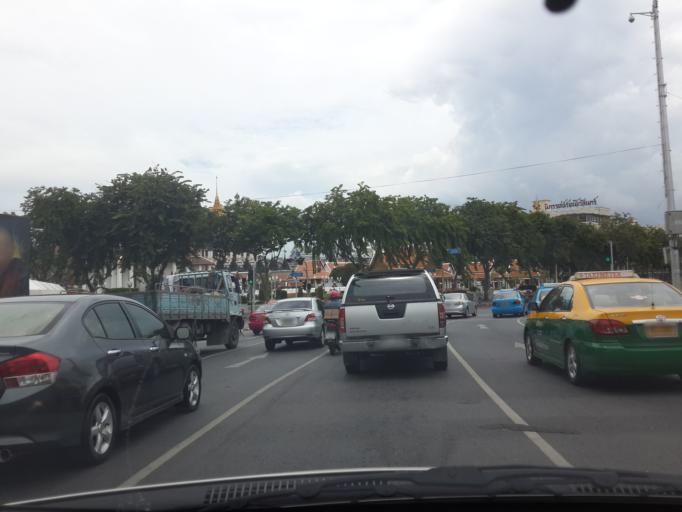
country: TH
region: Bangkok
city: Bangkok
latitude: 13.7561
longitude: 100.5056
